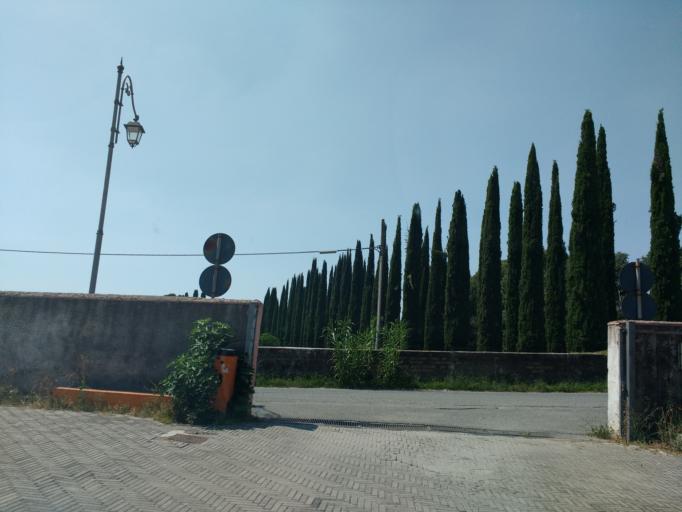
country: IT
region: Latium
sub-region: Citta metropolitana di Roma Capitale
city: Villa Adriana
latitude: 41.9470
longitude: 12.7736
